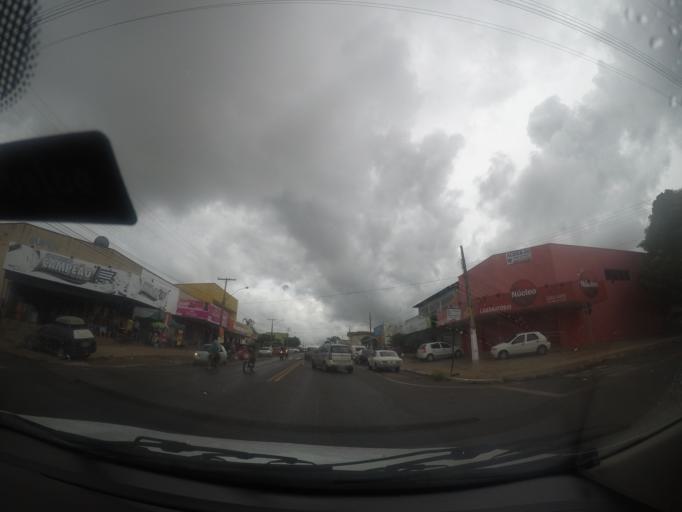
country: BR
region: Goias
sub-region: Trindade
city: Trindade
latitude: -16.6388
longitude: -49.3903
